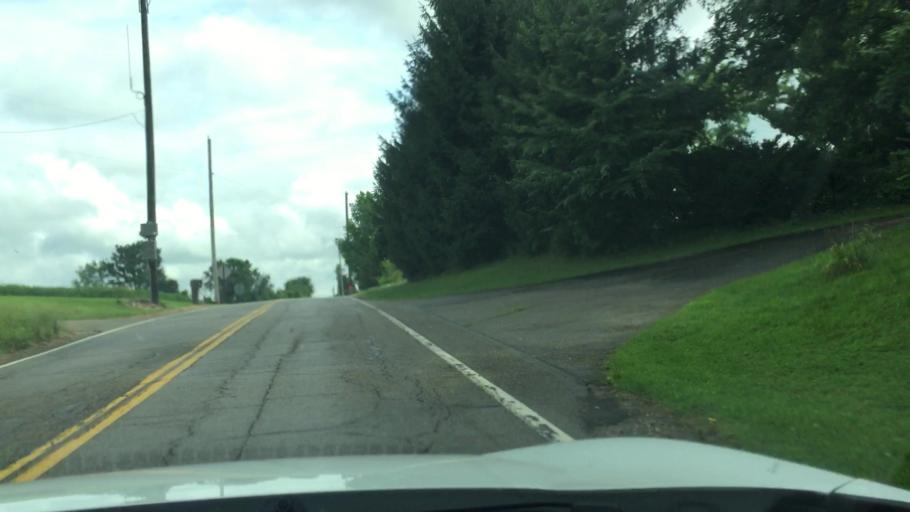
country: US
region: Ohio
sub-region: Clark County
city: Northridge
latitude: 40.0043
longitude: -83.6936
